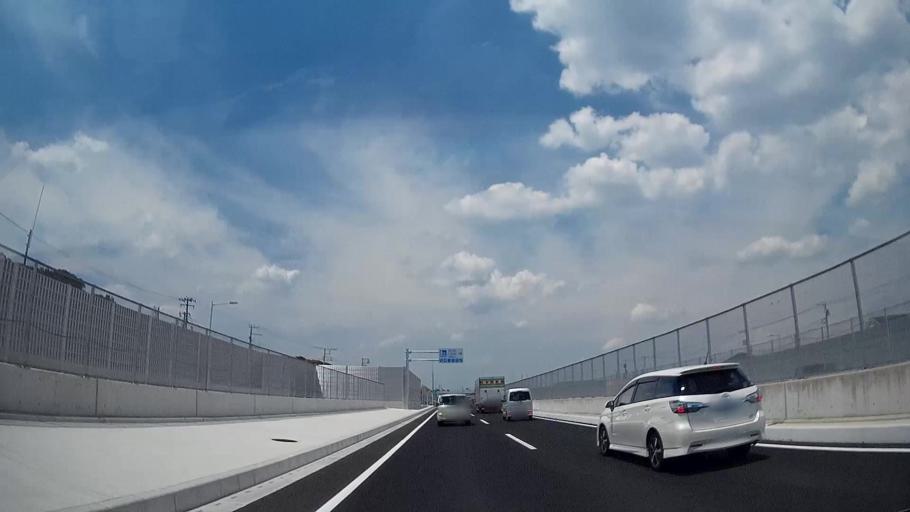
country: JP
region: Chiba
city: Matsudo
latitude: 35.7468
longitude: 139.9192
